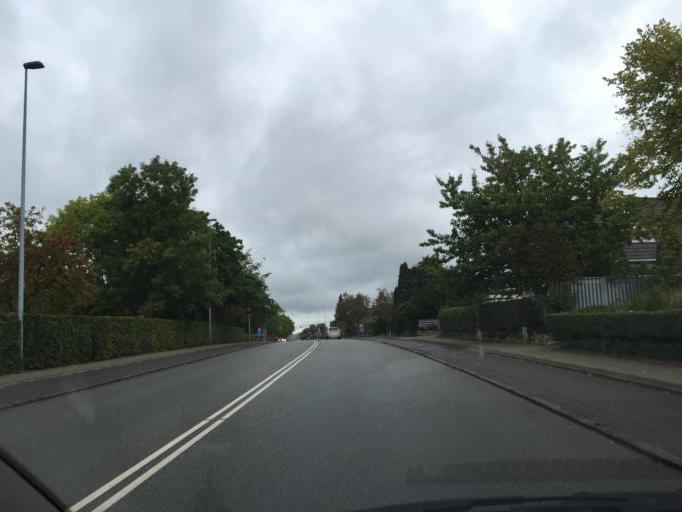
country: DK
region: Capital Region
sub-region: Gladsaxe Municipality
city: Buddinge
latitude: 55.7425
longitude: 12.4724
